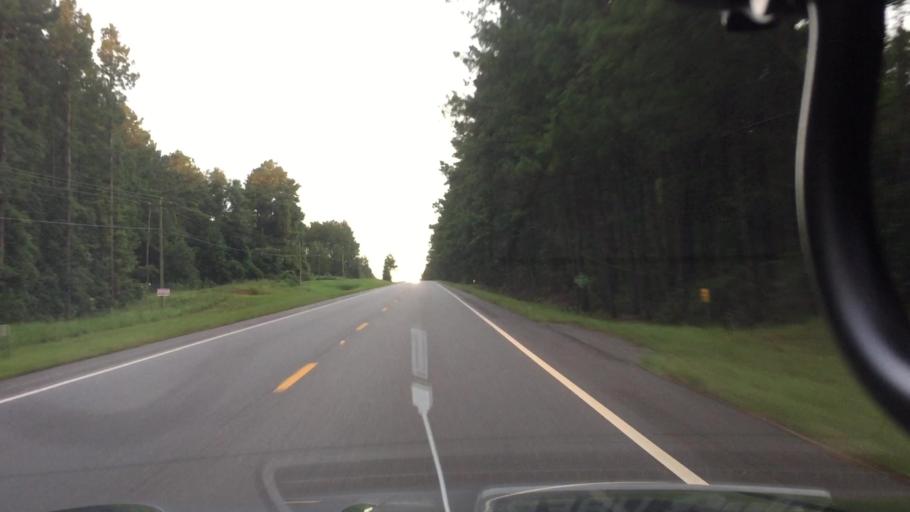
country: US
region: Alabama
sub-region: Coffee County
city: New Brockton
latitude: 31.5207
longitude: -85.9173
